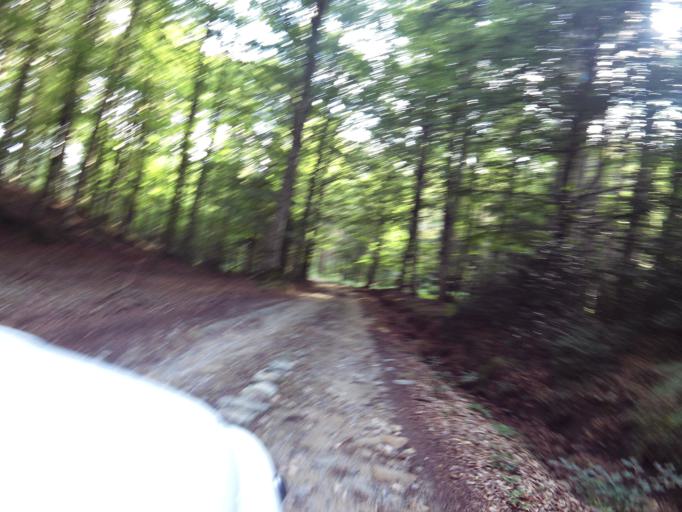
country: IT
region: Calabria
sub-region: Provincia di Vibo-Valentia
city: Nardodipace
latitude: 38.5175
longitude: 16.3798
